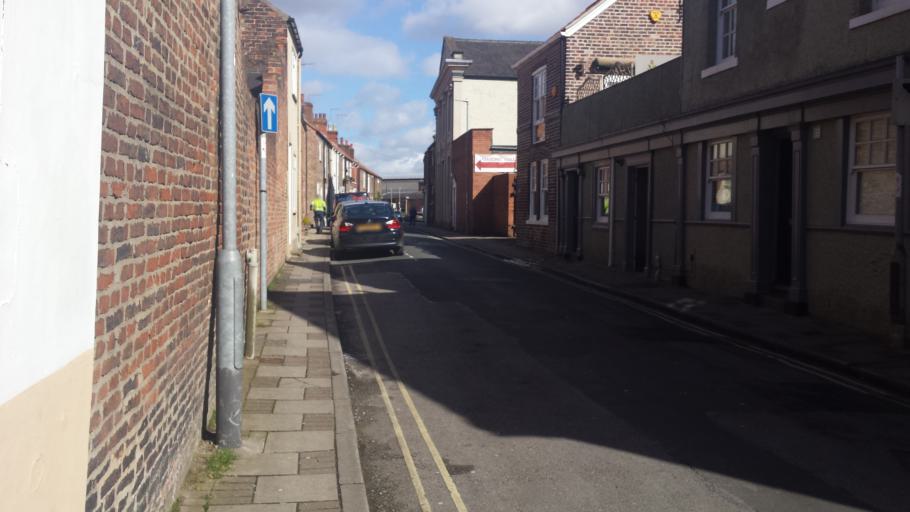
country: GB
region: England
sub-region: East Riding of Yorkshire
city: Beverley
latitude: 53.8411
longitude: -0.4257
